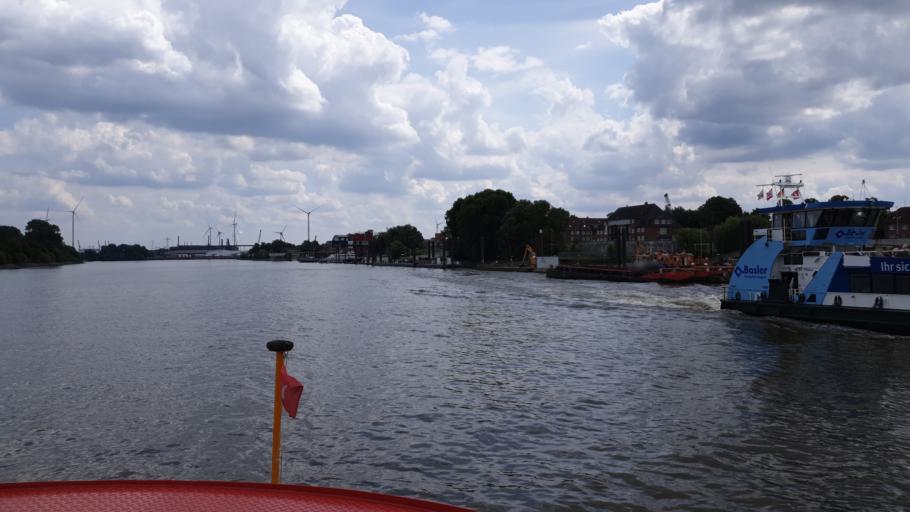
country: DE
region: Hamburg
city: Altona
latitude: 53.5388
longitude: 9.8767
